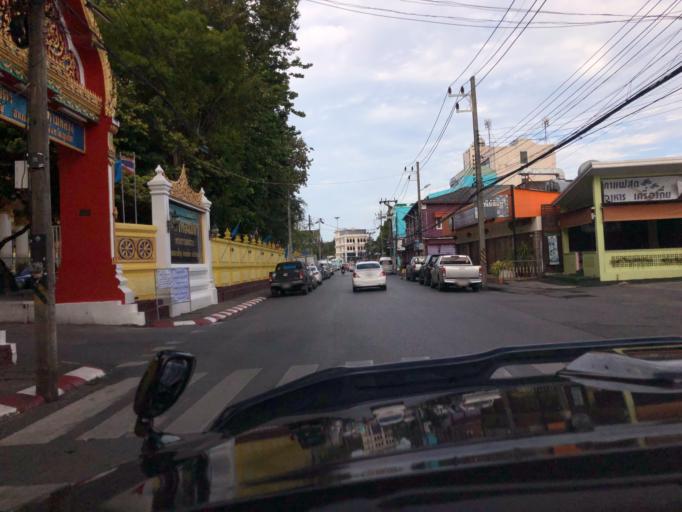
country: TH
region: Phuket
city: Ban Talat Nua
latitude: 7.8860
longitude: 98.3887
